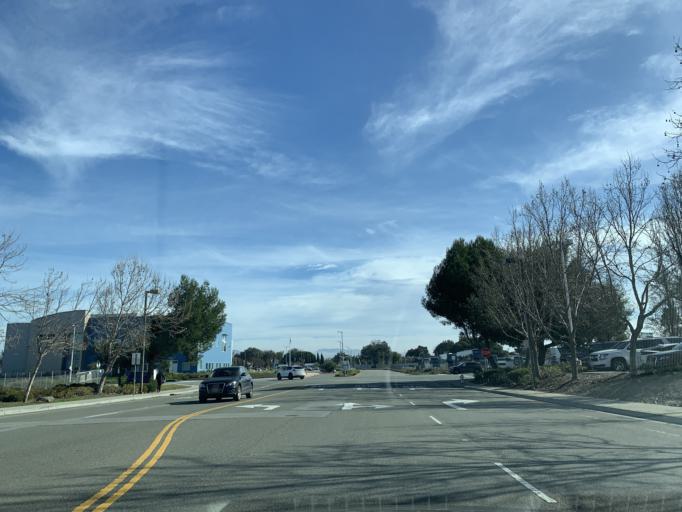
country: US
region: California
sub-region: Santa Clara County
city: Sunnyvale
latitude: 37.4046
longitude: -122.0306
